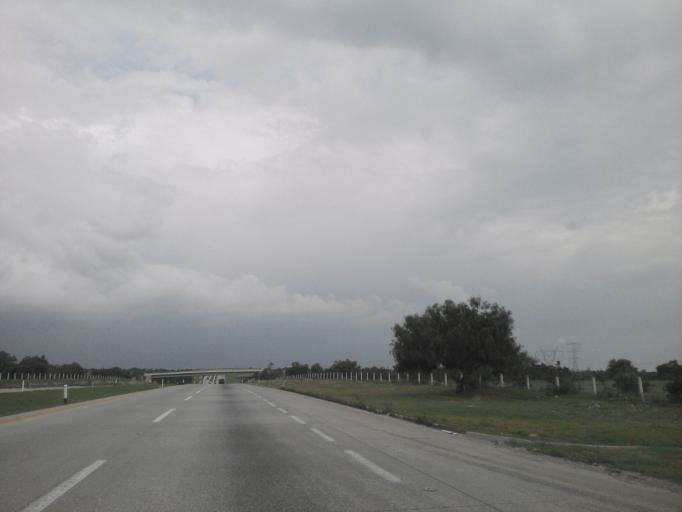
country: MX
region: Mexico
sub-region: Apaxco
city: Colonia Juarez
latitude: 19.9859
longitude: -99.1241
